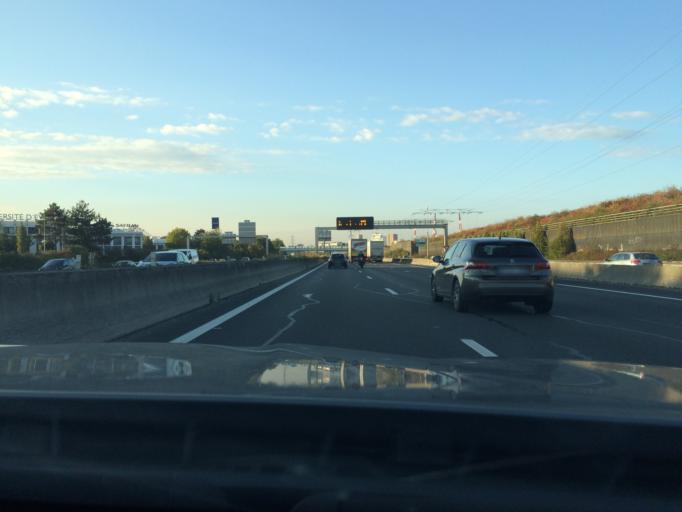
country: FR
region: Ile-de-France
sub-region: Departement de l'Essonne
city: Lisses
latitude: 48.6130
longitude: 2.4312
